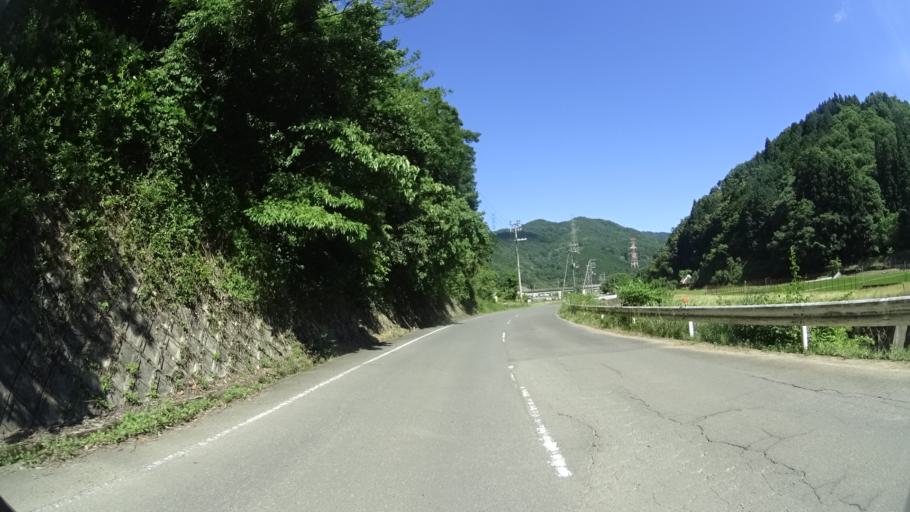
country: JP
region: Kyoto
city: Fukuchiyama
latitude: 35.3602
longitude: 135.1080
